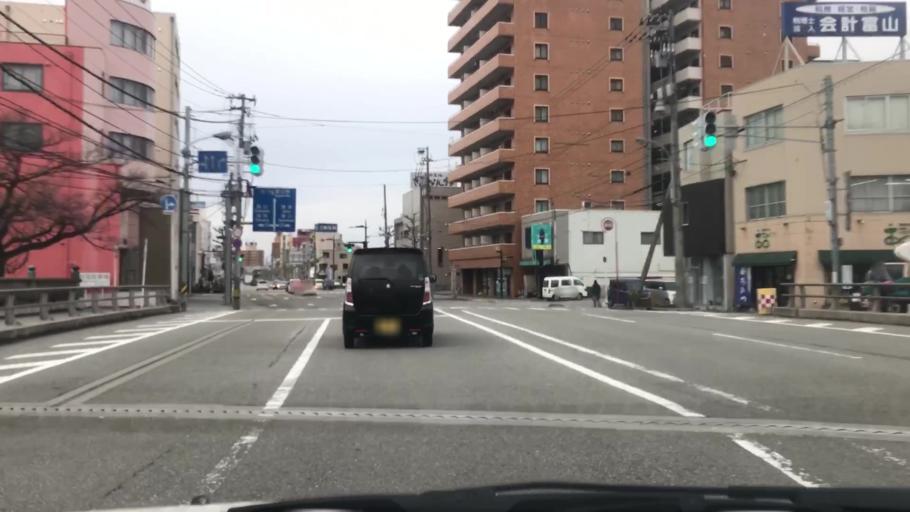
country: JP
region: Toyama
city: Toyama-shi
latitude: 36.6910
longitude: 137.2215
